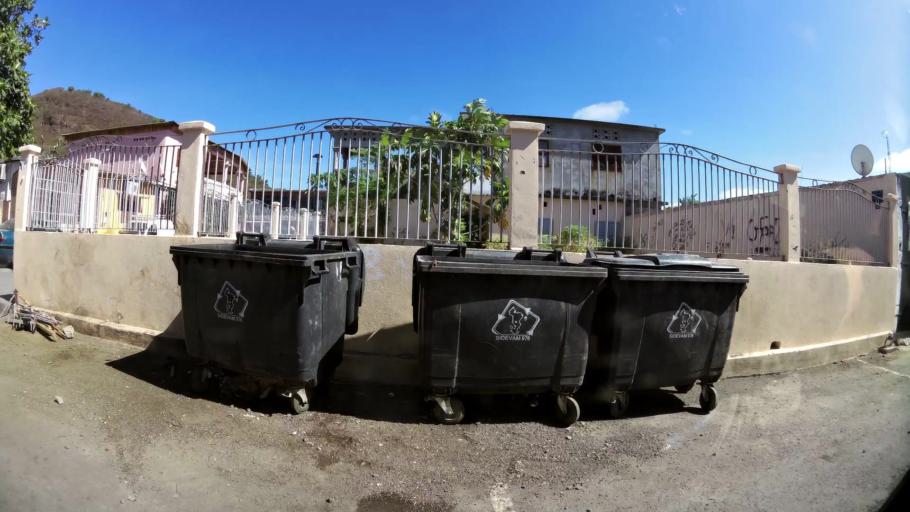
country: YT
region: Pamandzi
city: Pamandzi
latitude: -12.7871
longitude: 45.2744
